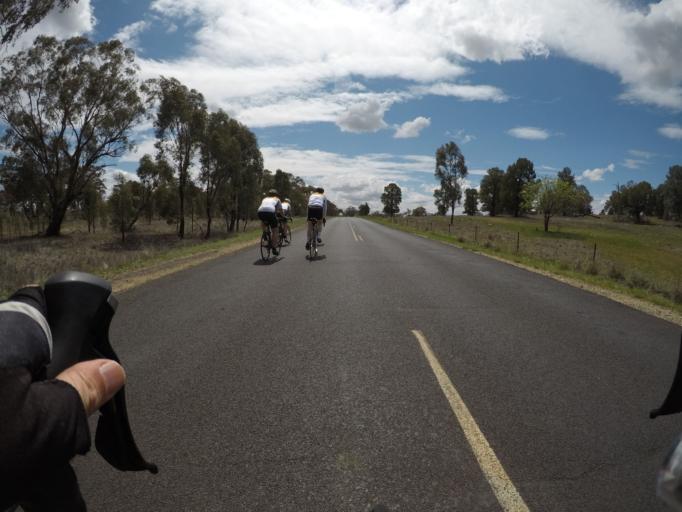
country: AU
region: New South Wales
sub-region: Dubbo Municipality
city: Dubbo
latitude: -32.2896
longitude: 148.5982
